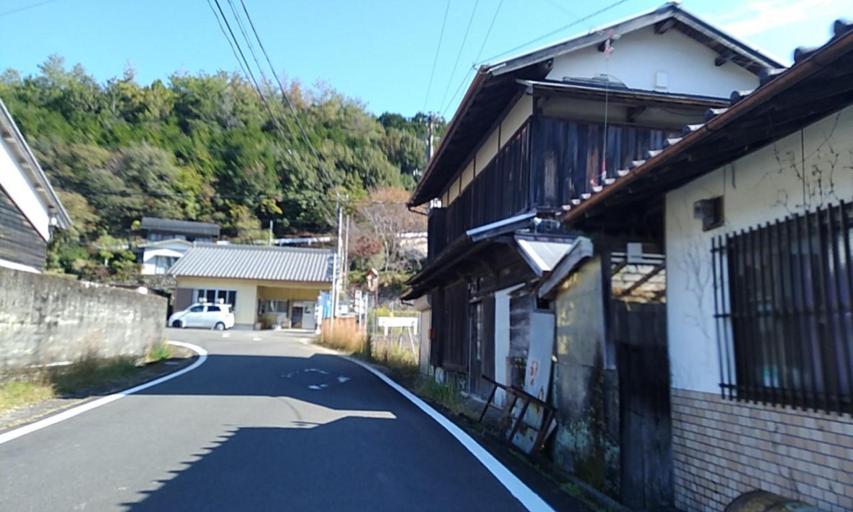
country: JP
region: Wakayama
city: Shingu
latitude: 33.9241
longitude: 135.9838
